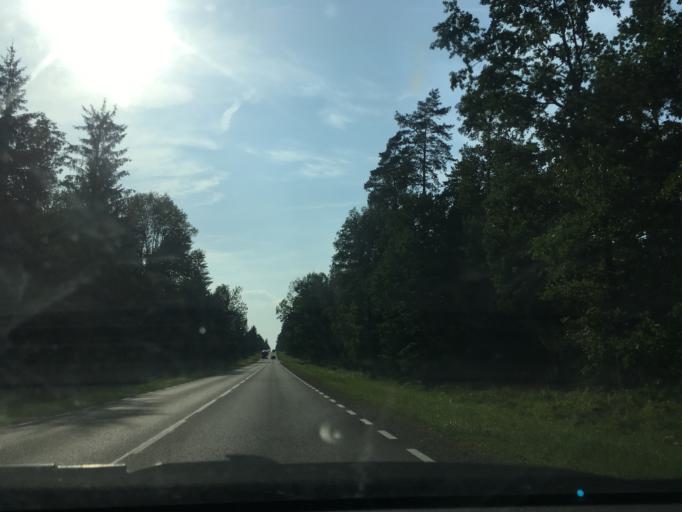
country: PL
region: Podlasie
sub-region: Powiat bialostocki
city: Suprasl
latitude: 53.1256
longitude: 23.3722
